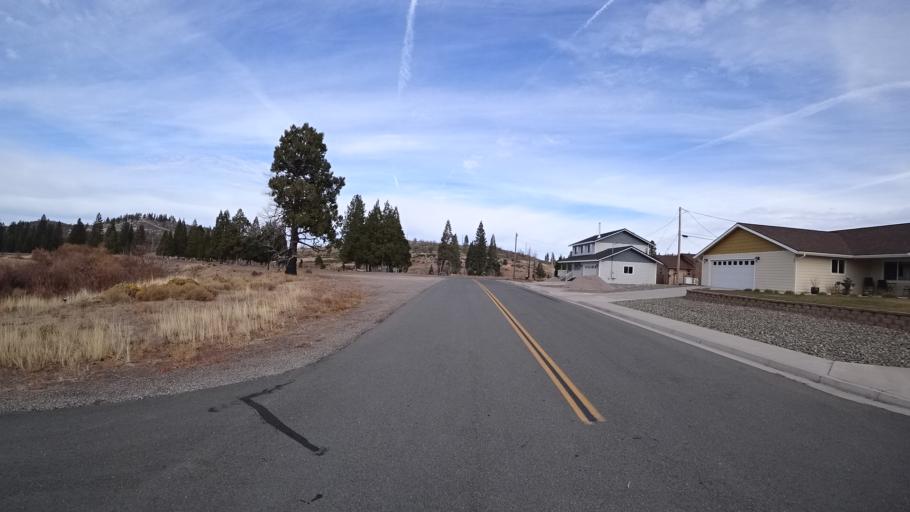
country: US
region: California
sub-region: Siskiyou County
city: Weed
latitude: 41.4386
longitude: -122.3814
